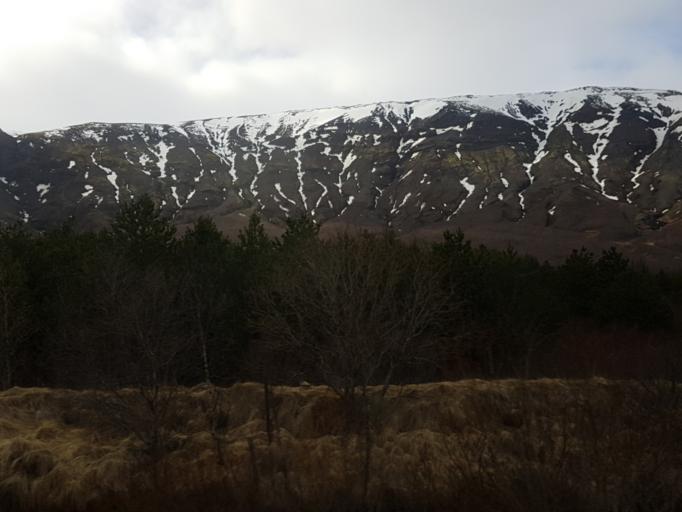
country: IS
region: South
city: Selfoss
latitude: 64.2286
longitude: -20.7185
